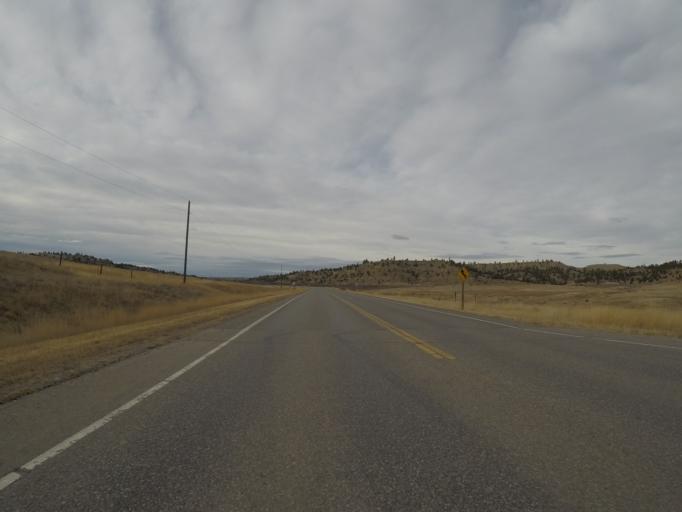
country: US
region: Montana
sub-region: Yellowstone County
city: Laurel
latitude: 45.8145
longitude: -108.6809
